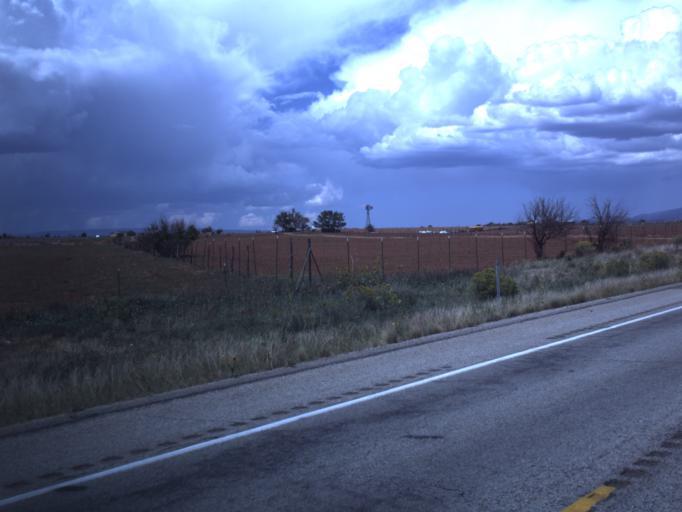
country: US
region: Utah
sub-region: San Juan County
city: Blanding
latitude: 37.5605
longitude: -109.4895
